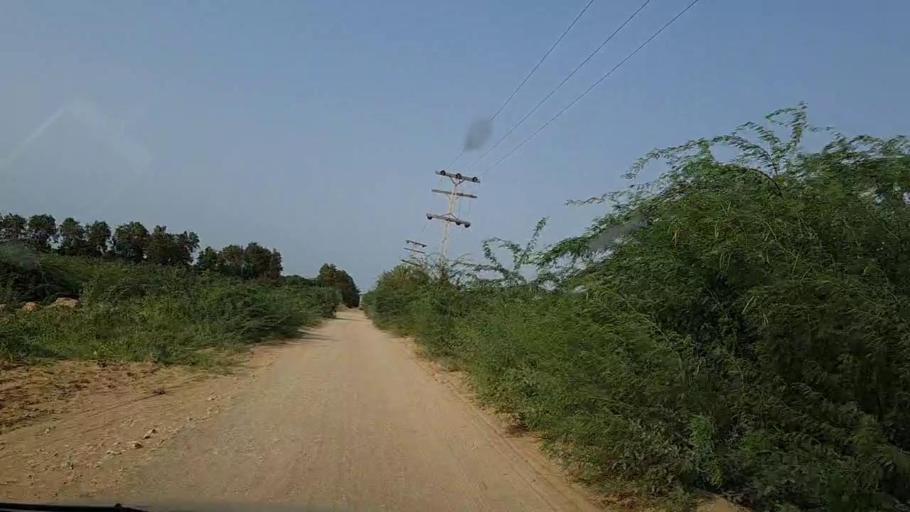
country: PK
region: Sindh
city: Kotri
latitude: 25.2234
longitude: 68.2493
